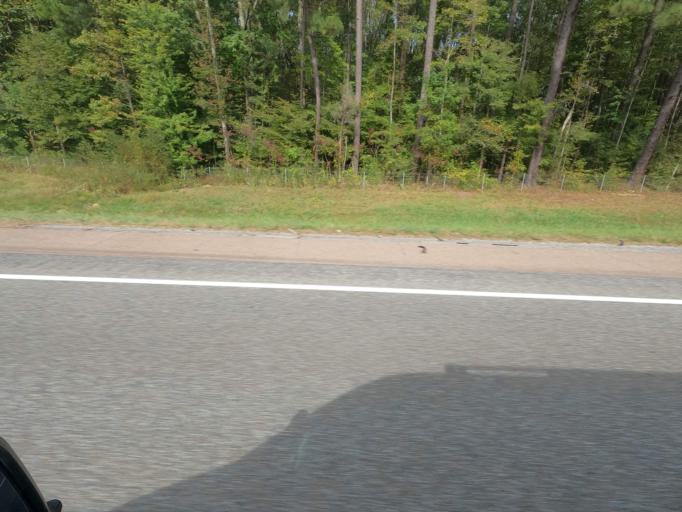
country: US
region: Tennessee
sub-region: Henderson County
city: Lexington
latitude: 35.8174
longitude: -88.2705
